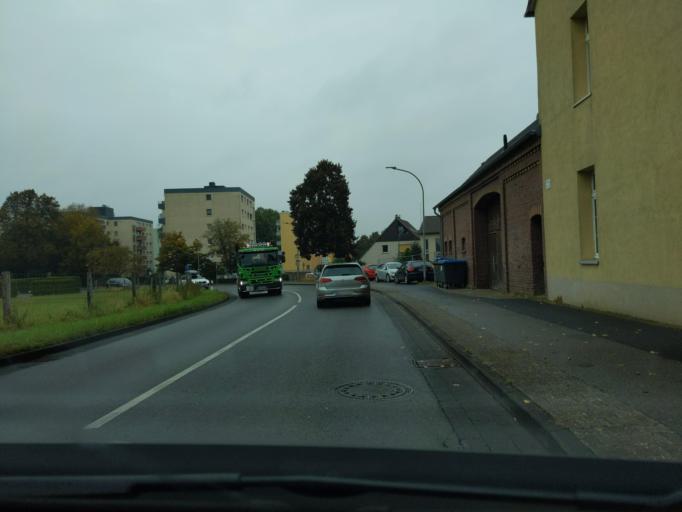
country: DE
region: North Rhine-Westphalia
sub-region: Regierungsbezirk Dusseldorf
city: Kaarst
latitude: 51.2151
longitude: 6.6109
